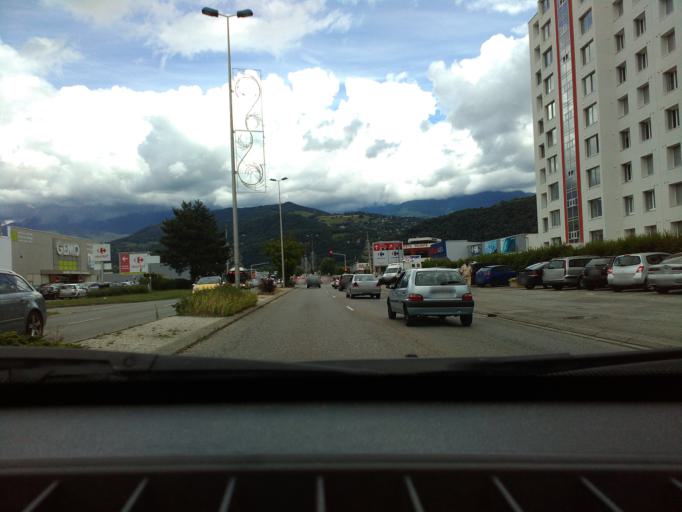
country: FR
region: Rhone-Alpes
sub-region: Departement de l'Isere
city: Saint-Martin-d'Heres
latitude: 45.1847
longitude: 5.7667
